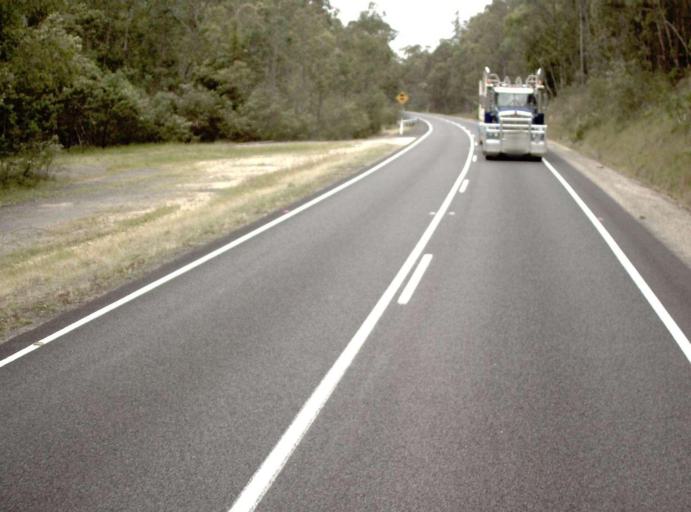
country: AU
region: New South Wales
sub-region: Bombala
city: Bombala
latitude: -37.3178
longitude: 149.2060
